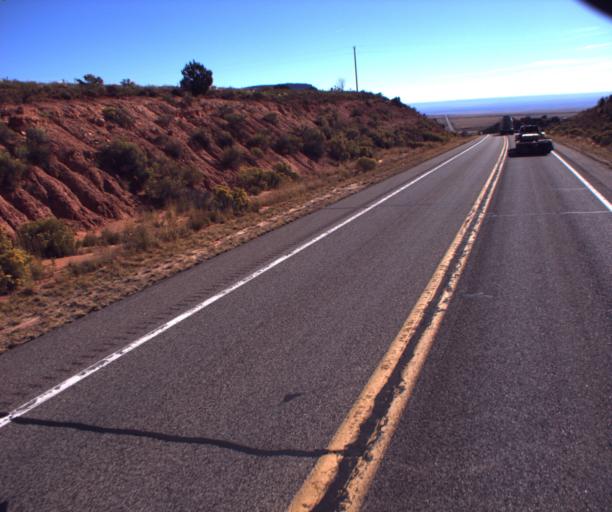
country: US
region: Arizona
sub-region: Mohave County
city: Colorado City
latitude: 36.8819
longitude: -112.8973
